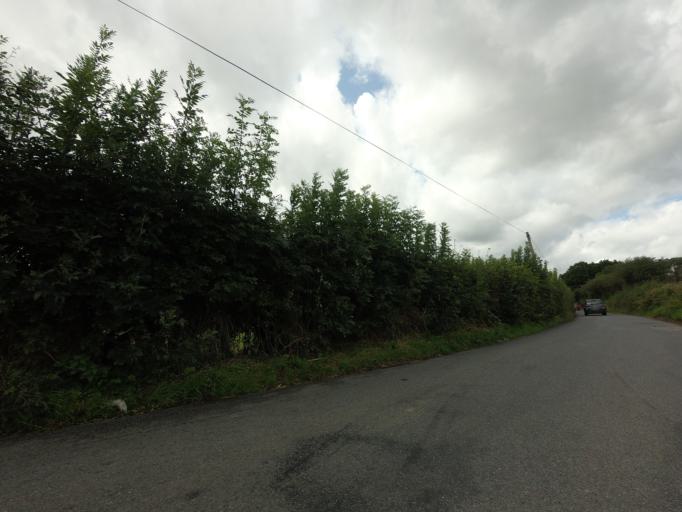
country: GB
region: England
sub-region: Kent
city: Hadlow
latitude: 51.2385
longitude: 0.3259
